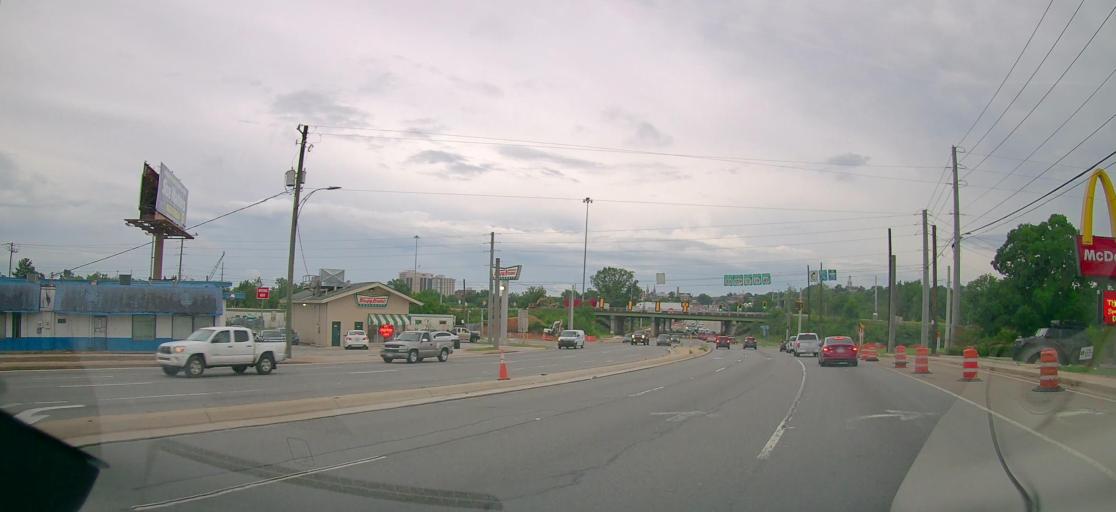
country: US
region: Georgia
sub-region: Bibb County
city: Macon
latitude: 32.8475
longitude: -83.6246
